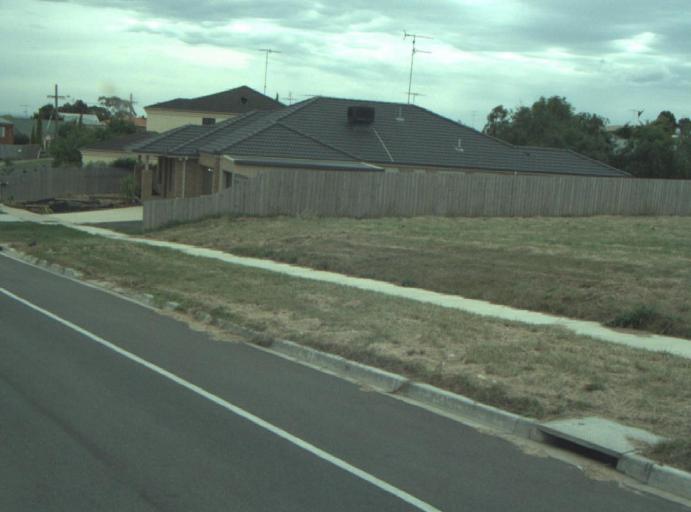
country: AU
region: Victoria
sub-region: Greater Geelong
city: Leopold
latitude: -38.1958
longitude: 144.4622
